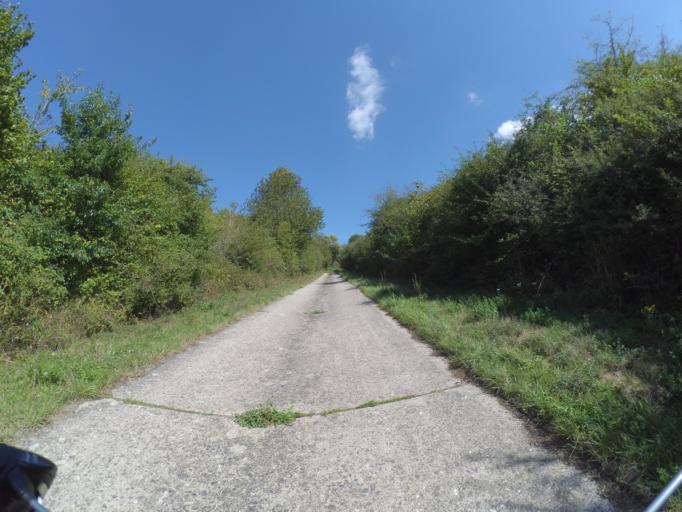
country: DE
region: Rheinland-Pfalz
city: Waldrach
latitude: 49.7555
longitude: 6.7618
